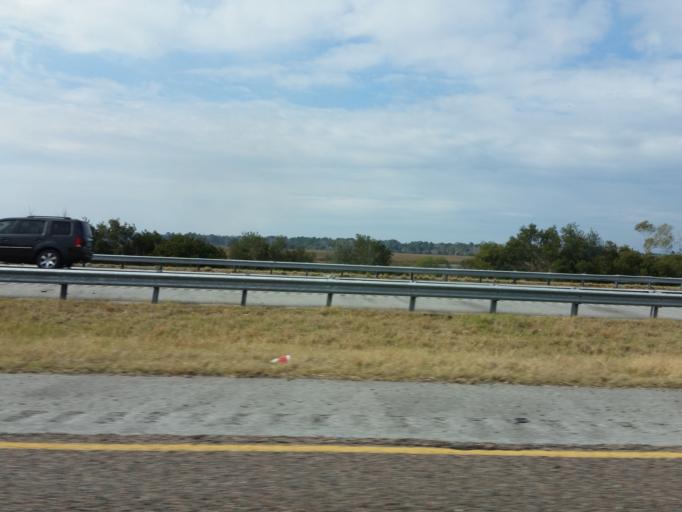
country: US
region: Georgia
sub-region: Liberty County
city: Midway
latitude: 31.8248
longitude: -81.3574
